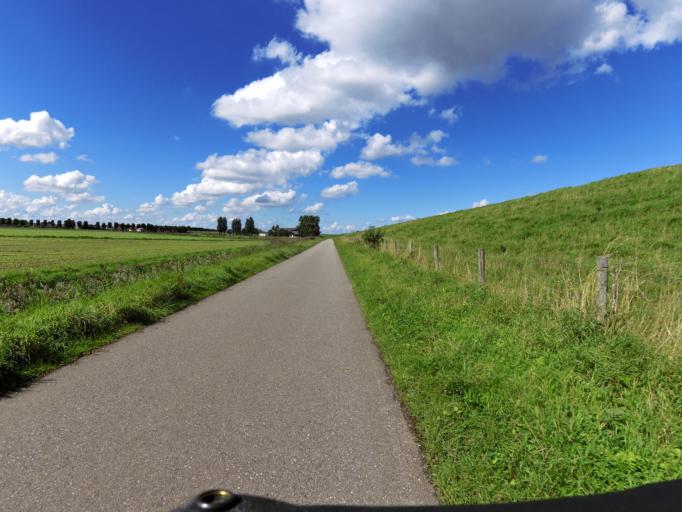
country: NL
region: North Brabant
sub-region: Gemeente Steenbergen
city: Dinteloord
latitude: 51.7147
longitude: 4.3002
